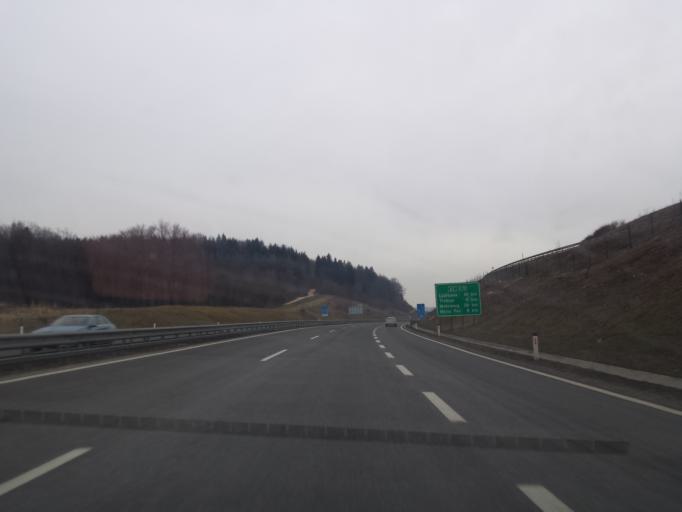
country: SI
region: Novo Mesto
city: Novo Mesto
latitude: 45.8462
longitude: 15.1494
